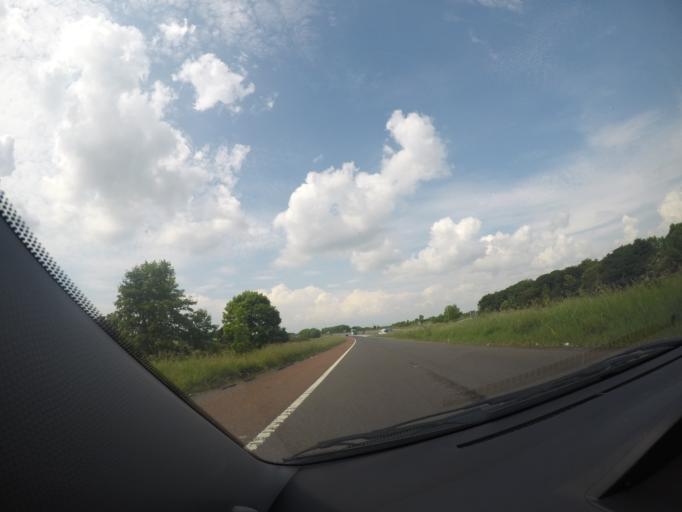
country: GB
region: England
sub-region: Cumbria
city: Scotby
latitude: 54.8002
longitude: -2.8718
